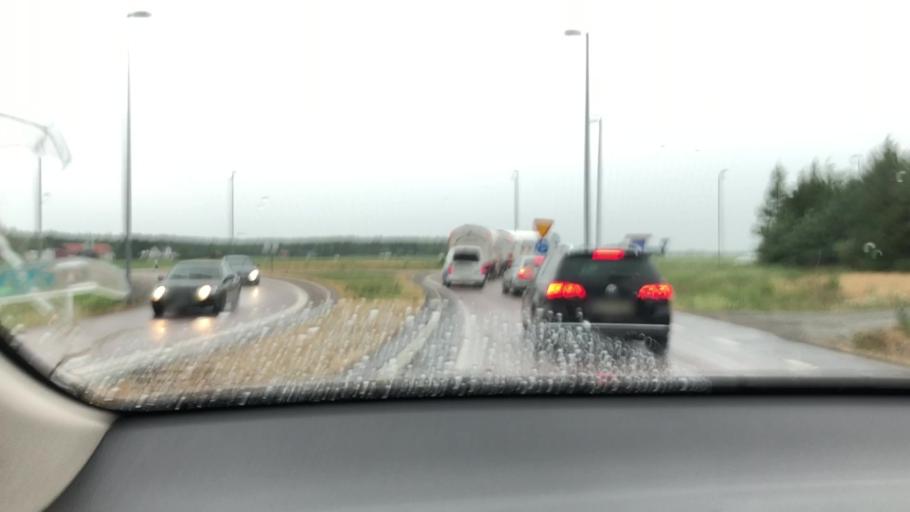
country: SE
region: Vaestmanland
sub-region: Sala Kommun
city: Sala
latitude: 59.8873
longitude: 16.6240
